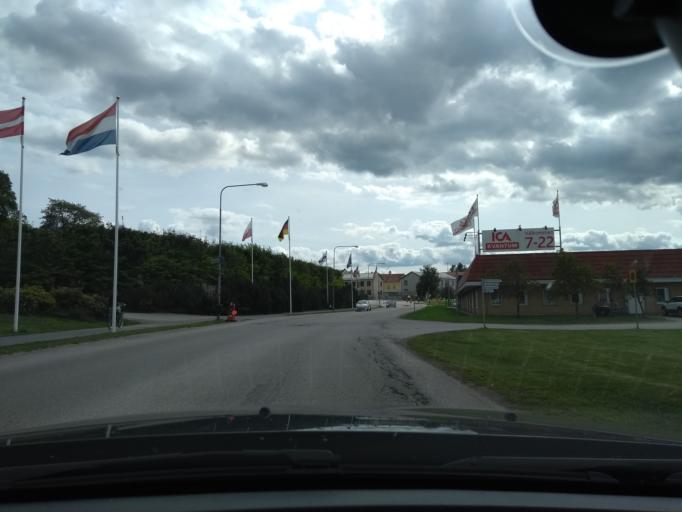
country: SE
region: Kalmar
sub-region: Vimmerby Kommun
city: Vimmerby
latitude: 57.6691
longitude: 15.8512
